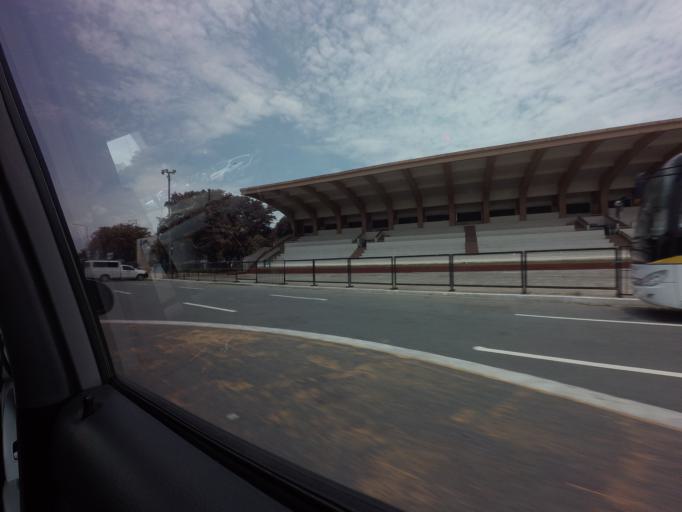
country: PH
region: Metro Manila
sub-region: City of Manila
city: Port Area
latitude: 14.5799
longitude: 120.9744
